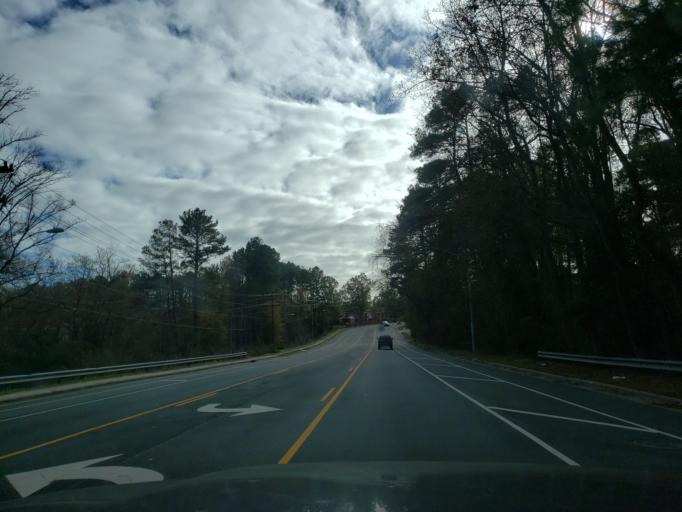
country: US
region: North Carolina
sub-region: Durham County
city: Durham
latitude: 35.9694
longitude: -78.9158
